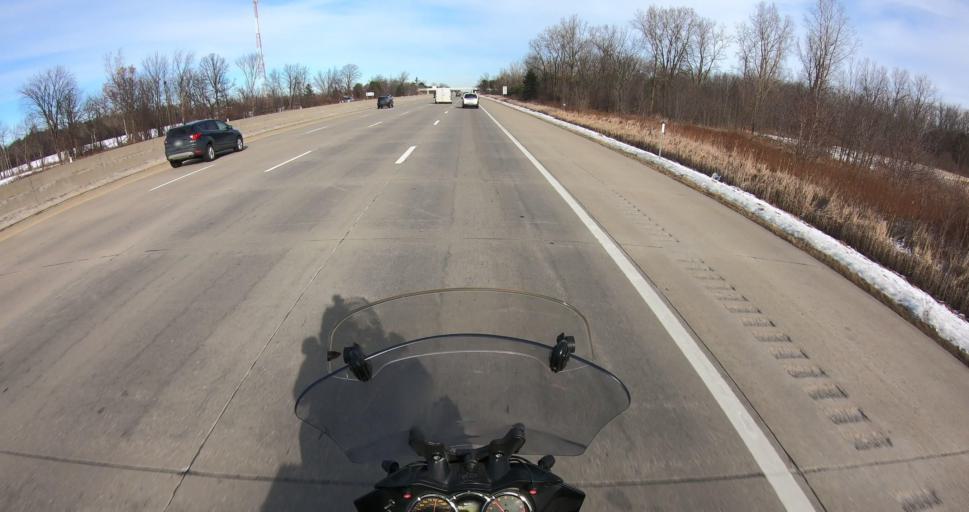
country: US
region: Michigan
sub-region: Genesee County
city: Clio
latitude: 43.1902
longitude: -83.7675
